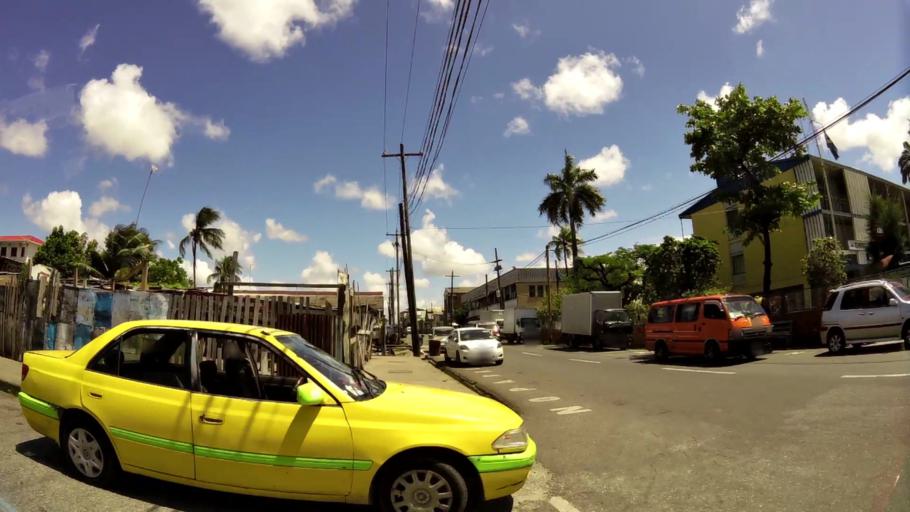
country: GY
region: Demerara-Mahaica
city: Georgetown
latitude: 6.8032
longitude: -58.1681
